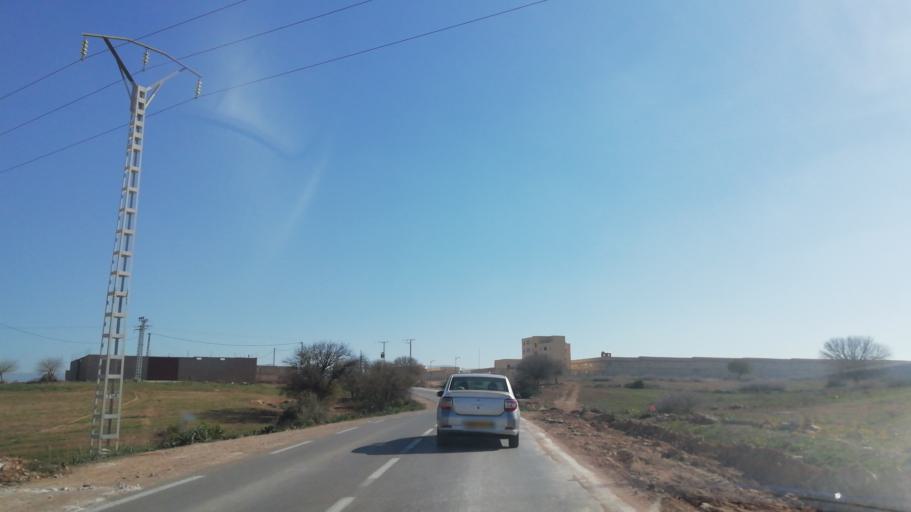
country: DZ
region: Tlemcen
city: Nedroma
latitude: 34.8342
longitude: -1.6844
